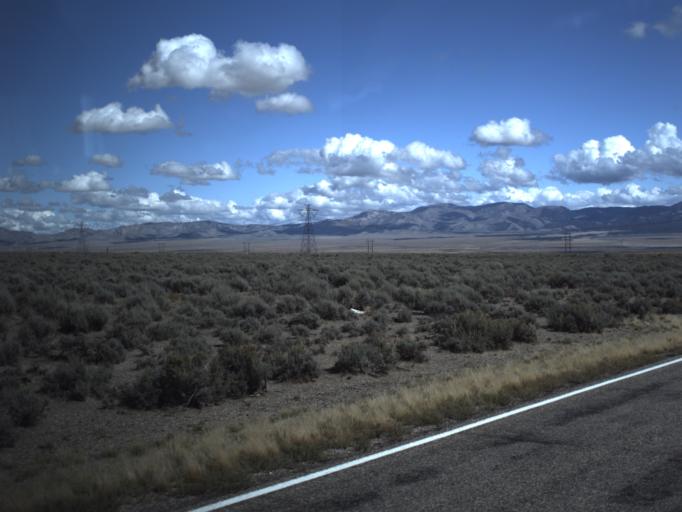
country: US
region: Utah
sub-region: Beaver County
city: Milford
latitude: 38.4125
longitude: -113.0709
